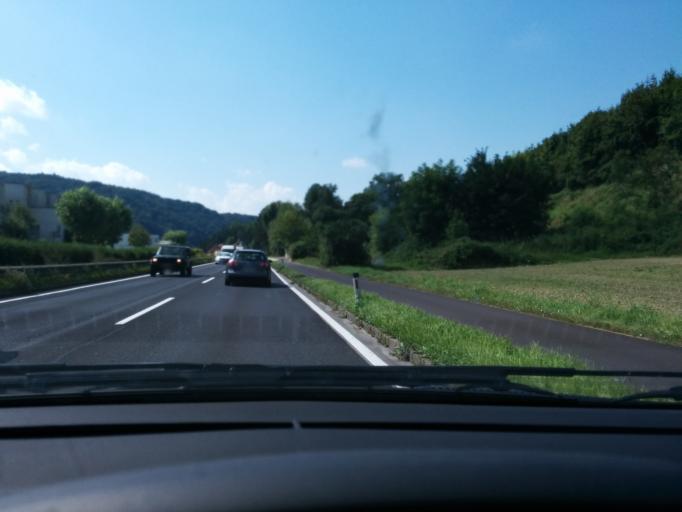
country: AT
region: Upper Austria
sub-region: Politischer Bezirk Linz-Land
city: Leonding
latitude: 48.3120
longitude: 14.2270
